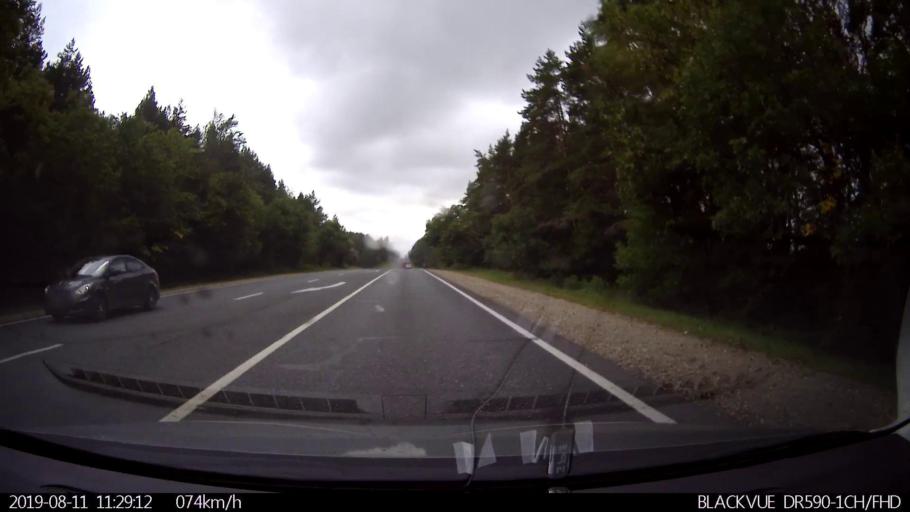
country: RU
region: Ulyanovsk
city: Krasnyy Gulyay
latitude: 54.0729
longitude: 48.2246
